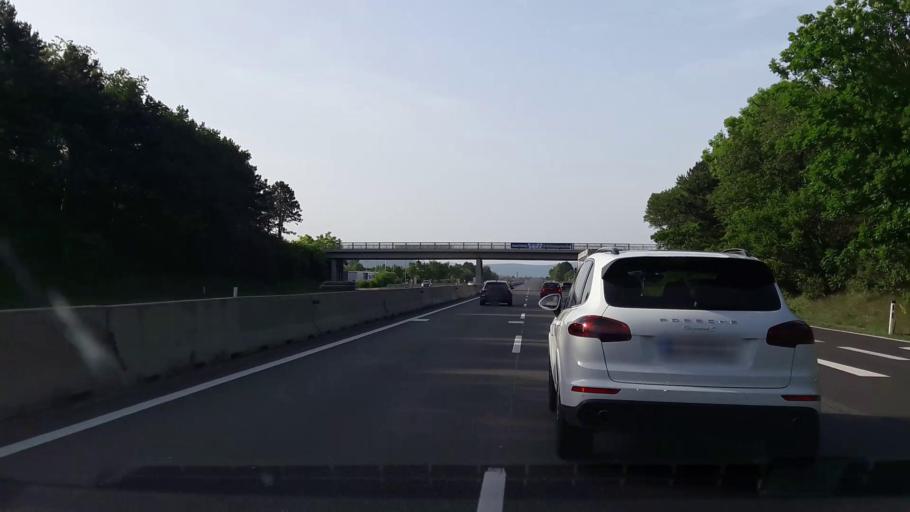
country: AT
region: Lower Austria
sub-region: Politischer Bezirk Baden
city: Leobersdorf
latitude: 47.9070
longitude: 16.2078
